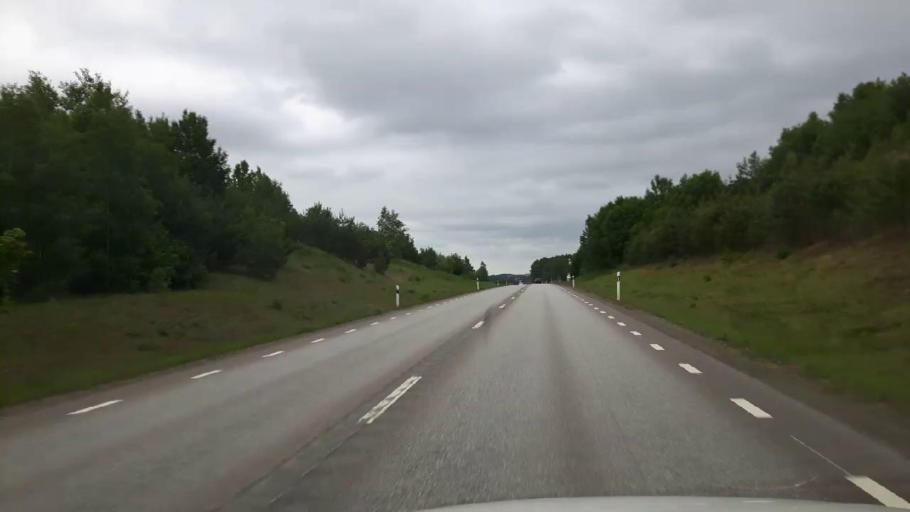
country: SE
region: Vaestmanland
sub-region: Kopings Kommun
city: Koping
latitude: 59.5421
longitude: 15.9357
